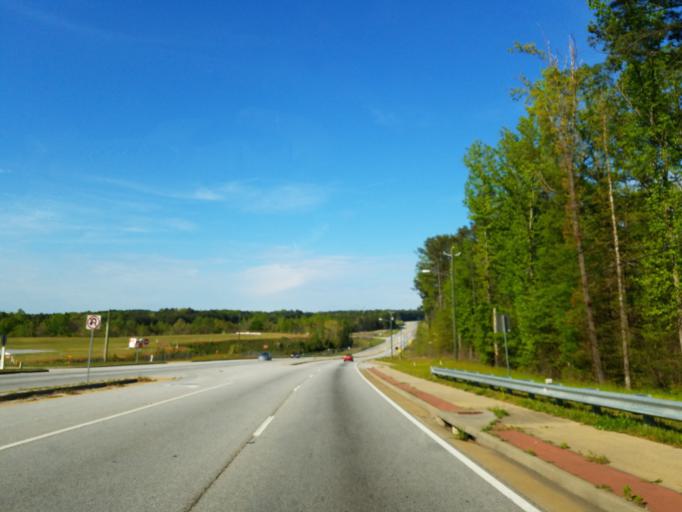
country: US
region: Georgia
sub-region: Cobb County
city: Mableton
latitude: 33.7789
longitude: -84.5111
